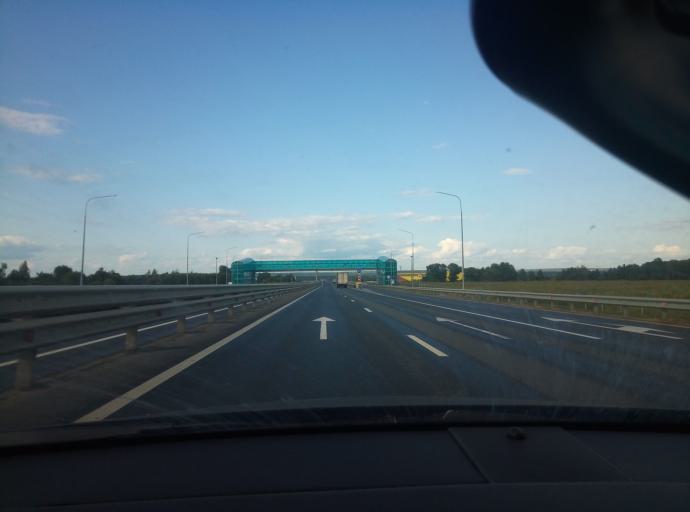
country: RU
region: Kaluga
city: Kurovskoye
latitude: 54.5383
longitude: 36.0033
